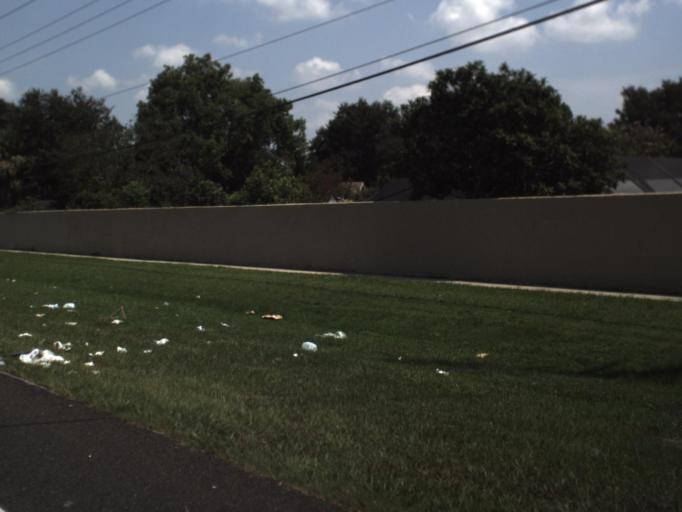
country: US
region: Florida
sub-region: Hillsborough County
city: Greater Northdale
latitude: 28.1072
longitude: -82.5023
